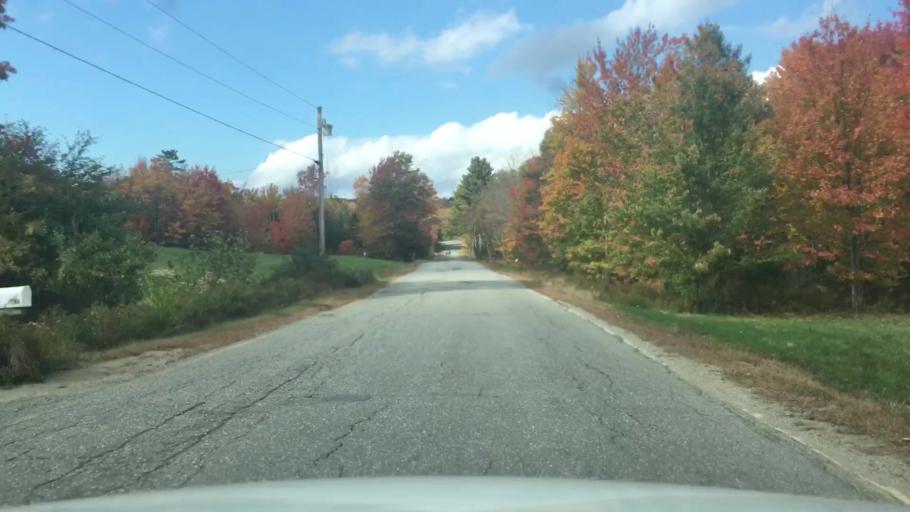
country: US
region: Maine
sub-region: Knox County
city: Washington
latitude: 44.3329
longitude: -69.3704
